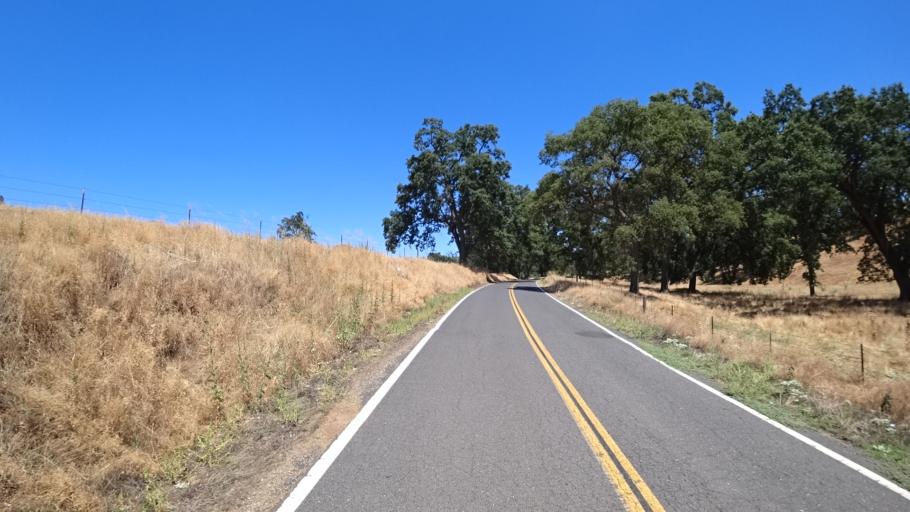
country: US
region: California
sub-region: Calaveras County
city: Murphys
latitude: 38.1213
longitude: -120.5091
